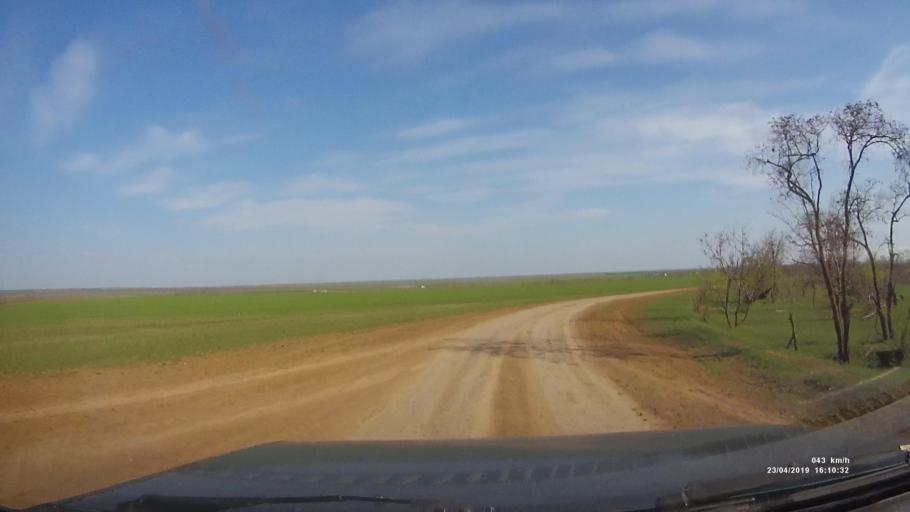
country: RU
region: Rostov
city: Remontnoye
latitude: 46.4813
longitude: 43.1228
